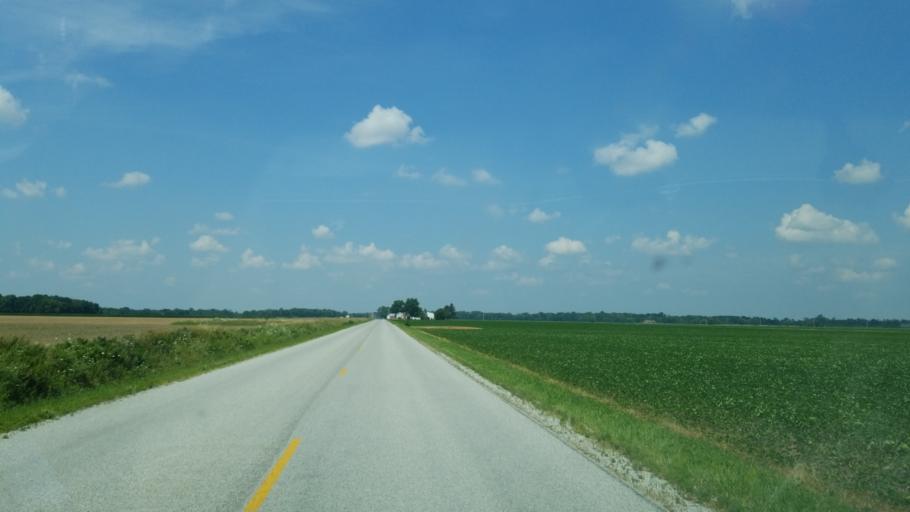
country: US
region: Ohio
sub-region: Seneca County
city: Fostoria
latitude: 41.2387
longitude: -83.5042
